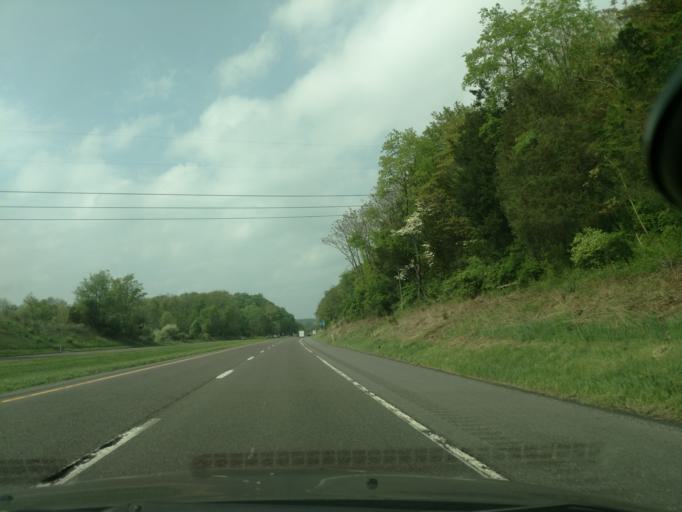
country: US
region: Pennsylvania
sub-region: Berks County
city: Flying Hills
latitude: 40.2436
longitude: -75.9154
